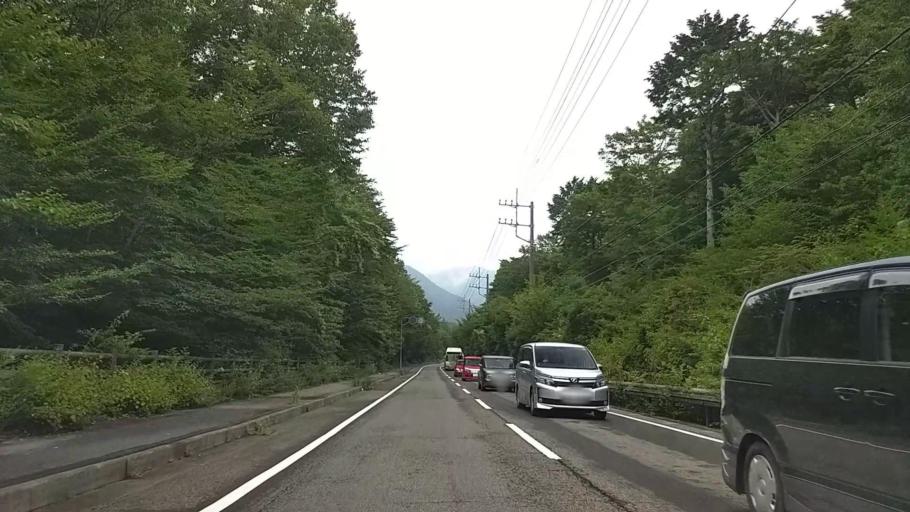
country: JP
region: Yamanashi
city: Fujikawaguchiko
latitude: 35.4818
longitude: 138.6548
